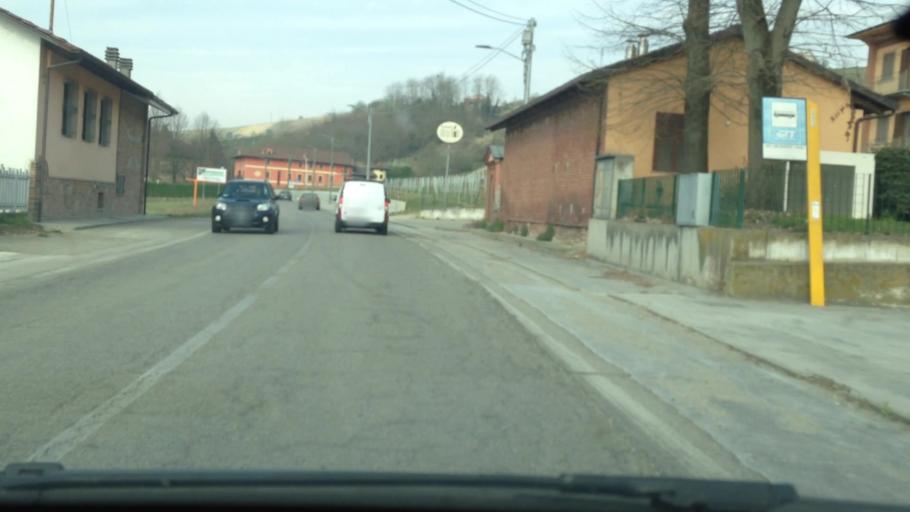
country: IT
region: Piedmont
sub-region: Provincia di Cuneo
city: Castellinaldo
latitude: 44.8059
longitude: 8.0270
